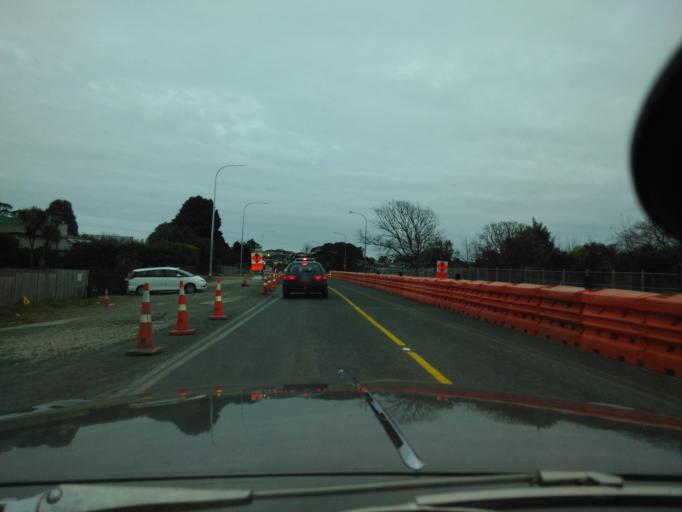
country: NZ
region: Auckland
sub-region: Auckland
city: Rothesay Bay
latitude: -36.7485
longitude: 174.6935
